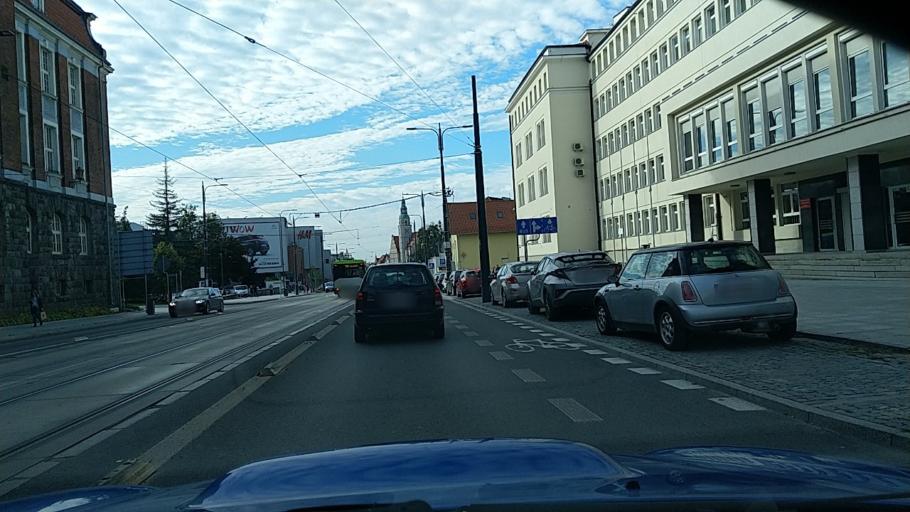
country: PL
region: Warmian-Masurian Voivodeship
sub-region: Powiat olsztynski
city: Olsztyn
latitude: 53.7768
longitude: 20.4868
